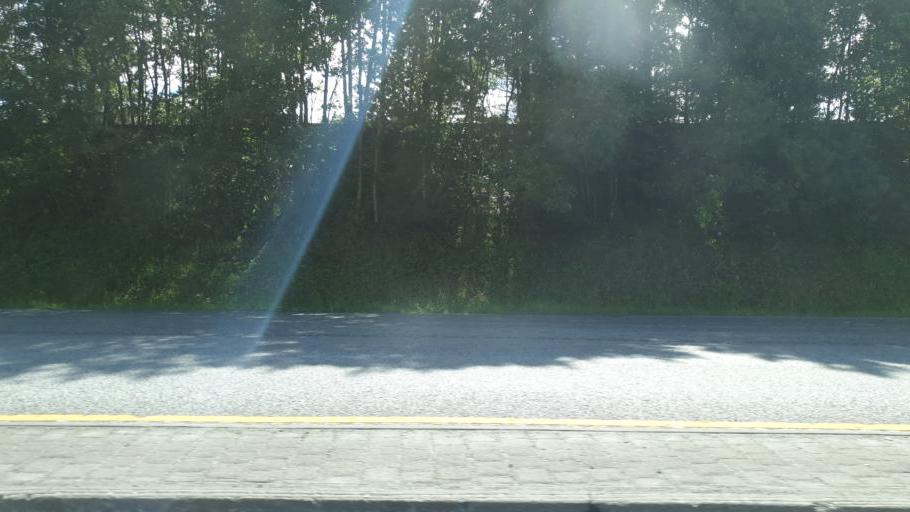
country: NO
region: Sor-Trondelag
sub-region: Midtre Gauldal
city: Storen
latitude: 63.0354
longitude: 10.2936
